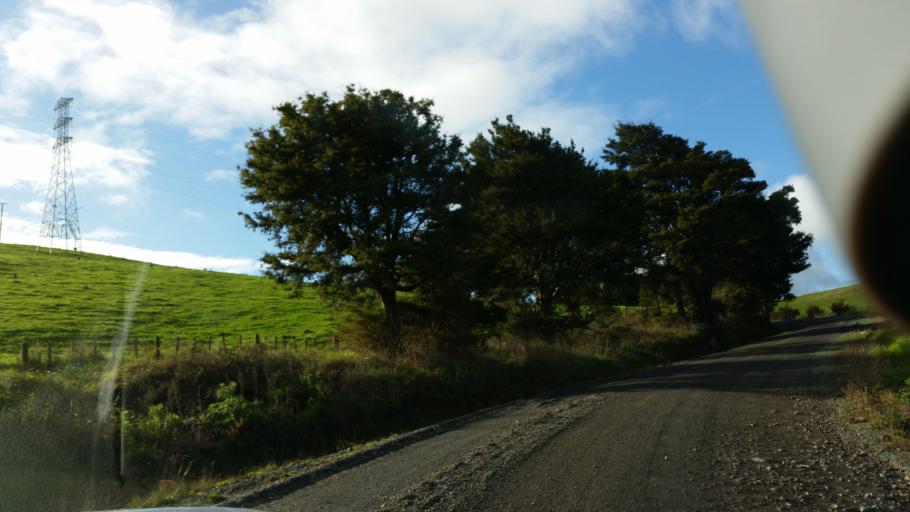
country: NZ
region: Northland
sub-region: Whangarei
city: Maungatapere
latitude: -35.6927
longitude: 174.1107
